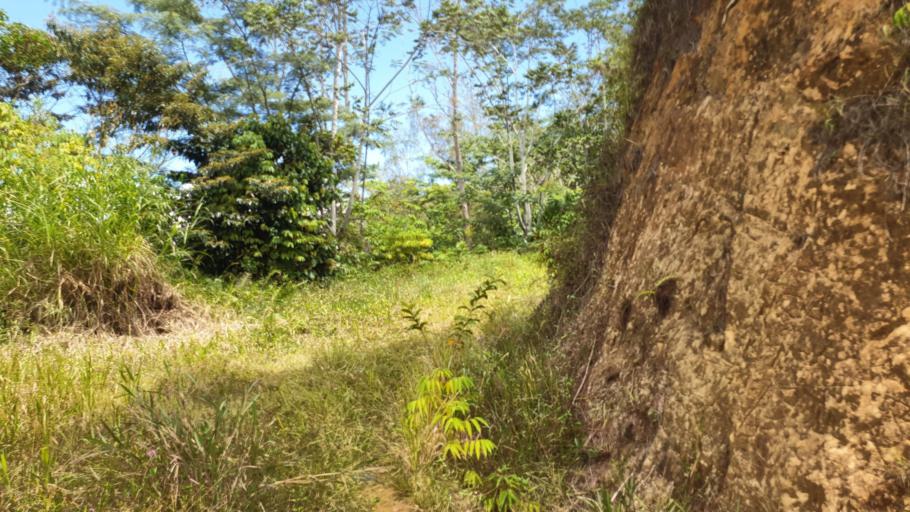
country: PG
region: Jiwaka
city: Minj
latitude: -5.9143
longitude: 144.8275
